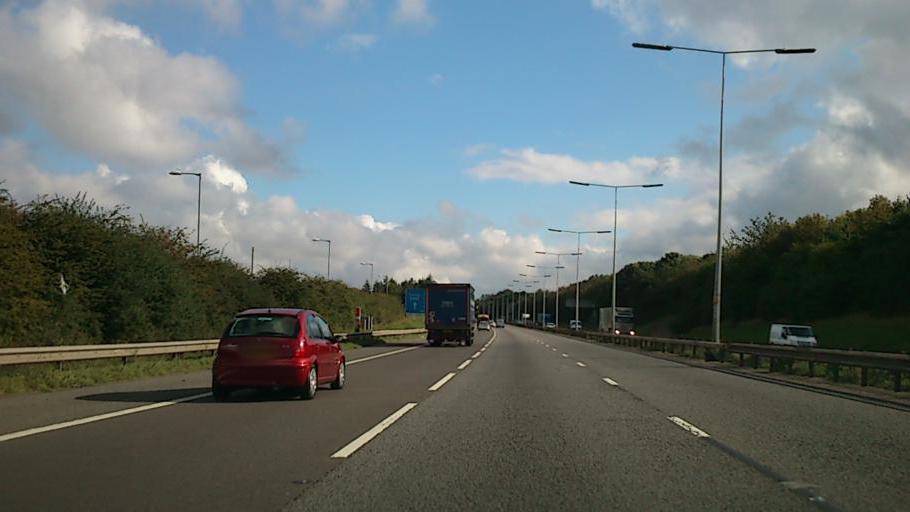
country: GB
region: England
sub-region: Staffordshire
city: Featherstone
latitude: 52.6384
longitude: -2.1077
